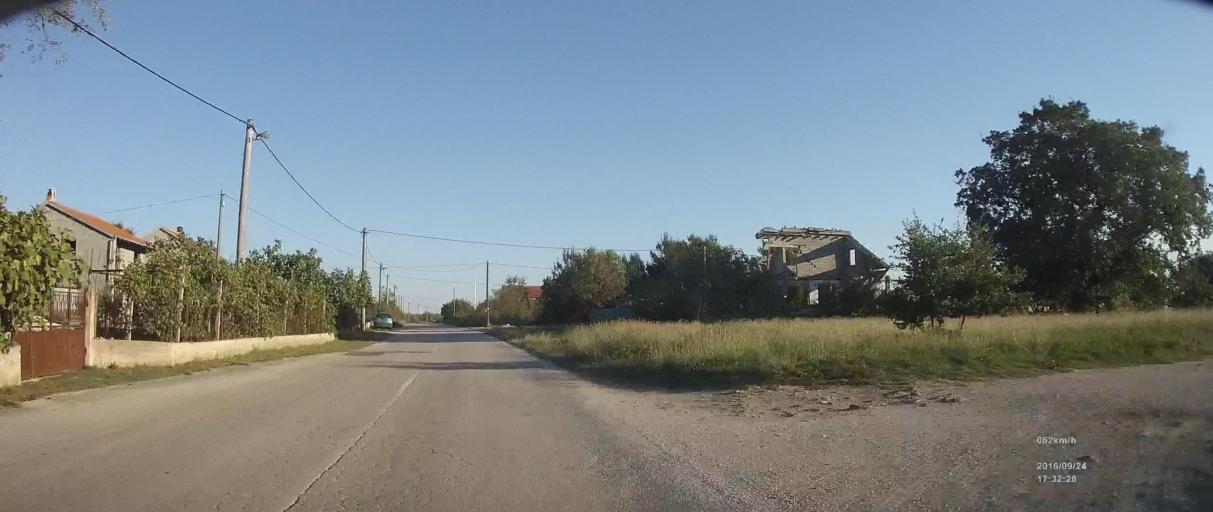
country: HR
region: Zadarska
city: Posedarje
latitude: 44.1820
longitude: 15.4505
